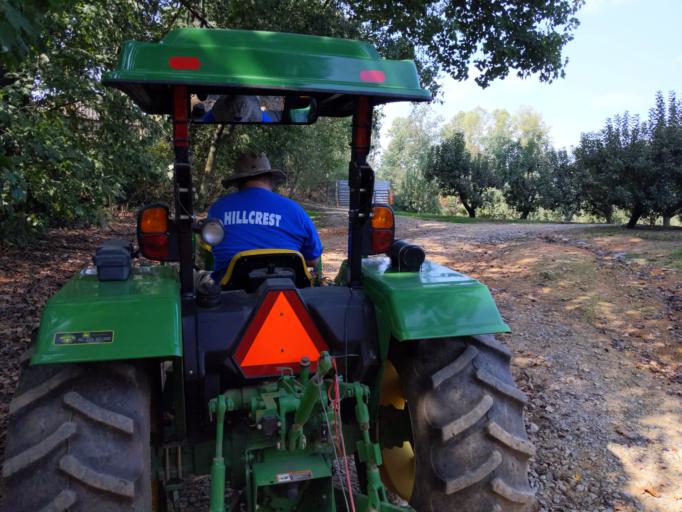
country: US
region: Georgia
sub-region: Gilmer County
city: Ellijay
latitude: 34.6183
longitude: -84.3745
